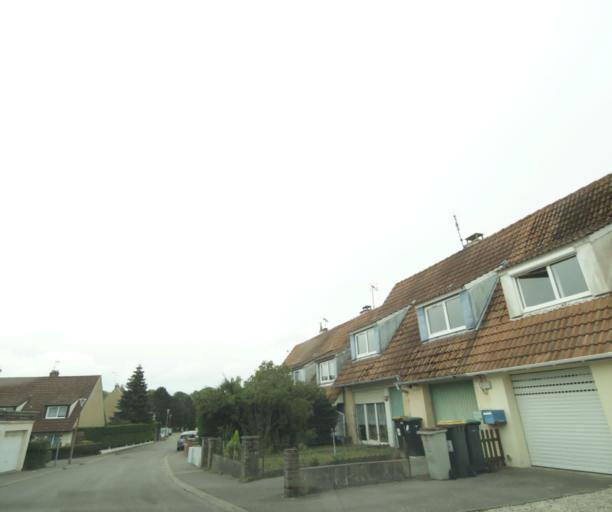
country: FR
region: Nord-Pas-de-Calais
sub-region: Departement du Pas-de-Calais
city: Etaples
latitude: 50.5231
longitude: 1.6457
